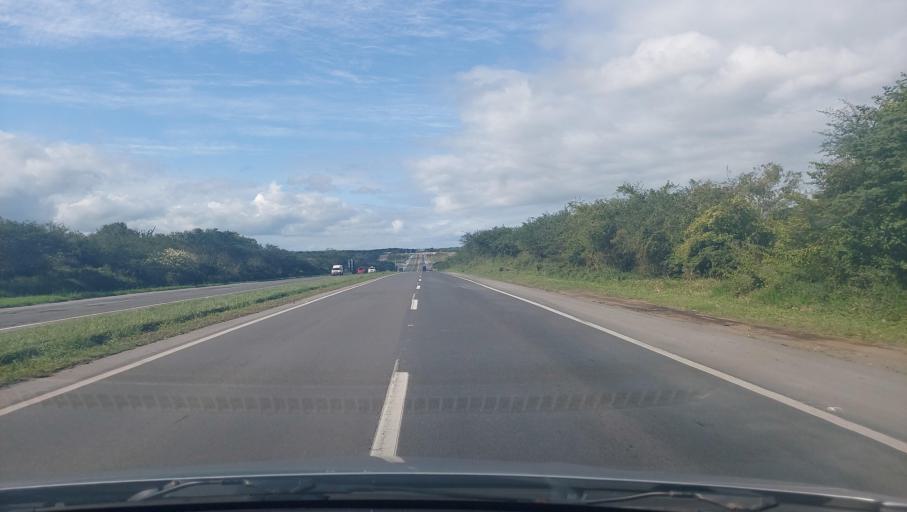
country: BR
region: Bahia
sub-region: Santo Estevao
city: Santo Estevao
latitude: -12.5066
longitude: -39.3631
